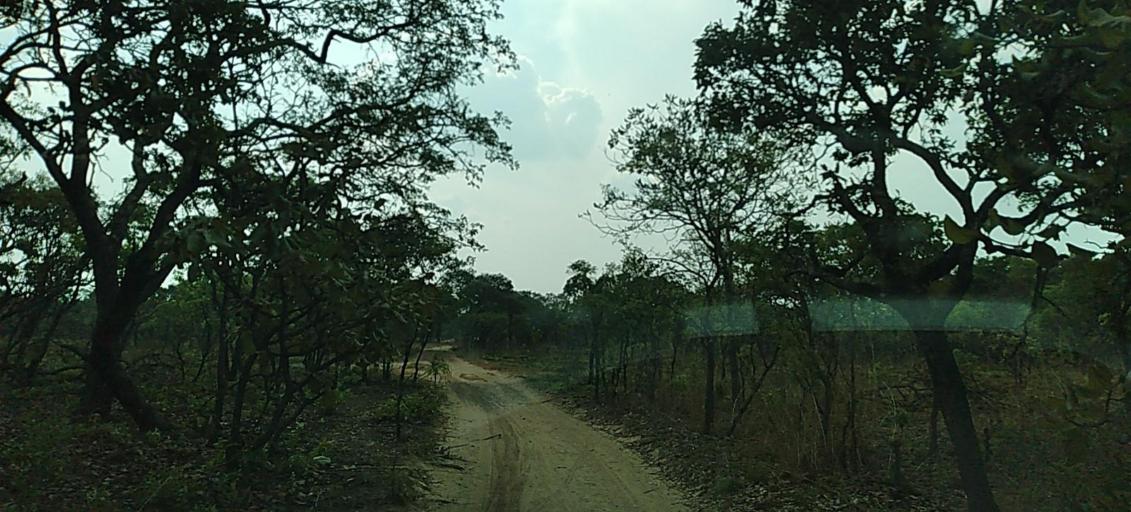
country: ZM
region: North-Western
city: Solwezi
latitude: -12.0770
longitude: 26.2412
